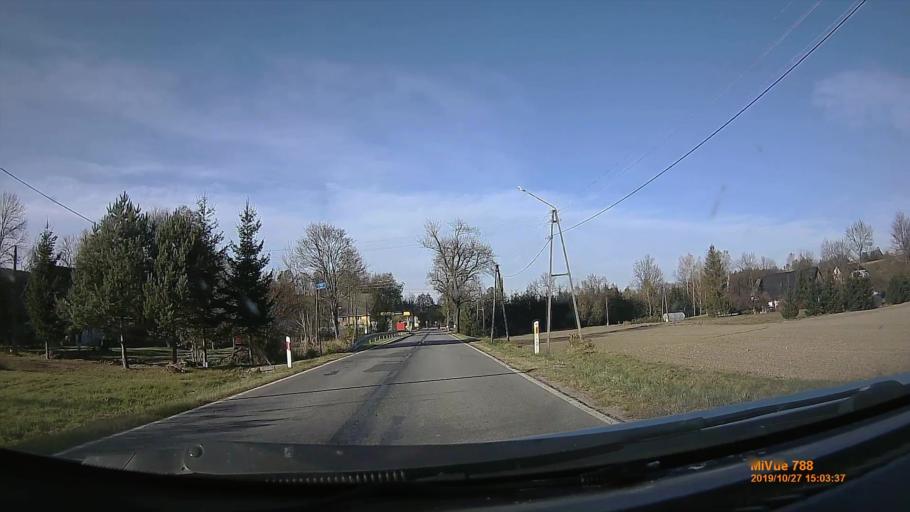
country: PL
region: Lower Silesian Voivodeship
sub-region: Powiat klodzki
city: Miedzylesie
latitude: 50.1335
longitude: 16.6640
